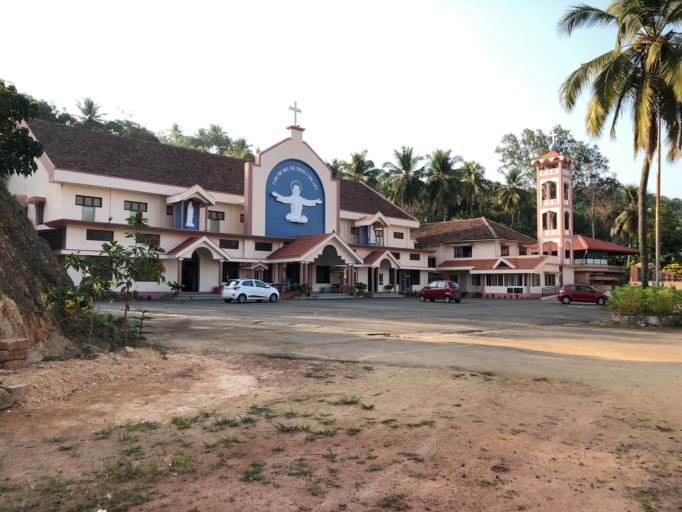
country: IN
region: Karnataka
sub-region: Dakshina Kannada
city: Mangalore
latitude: 12.8713
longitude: 74.8742
